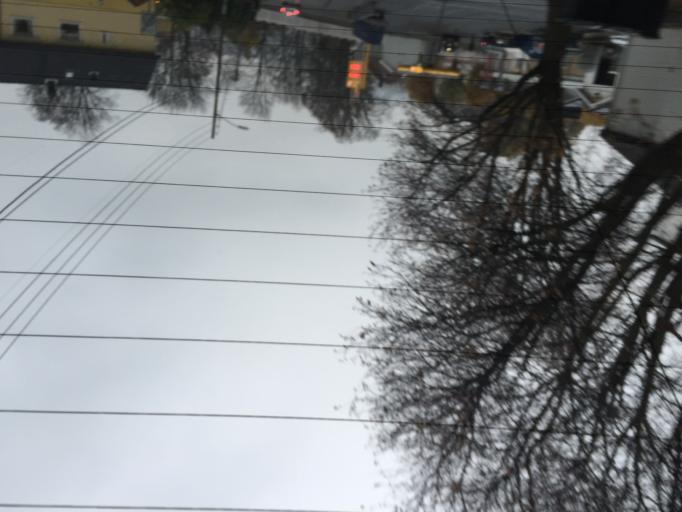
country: NO
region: Buskerud
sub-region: Drammen
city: Drammen
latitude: 59.7288
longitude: 10.2058
